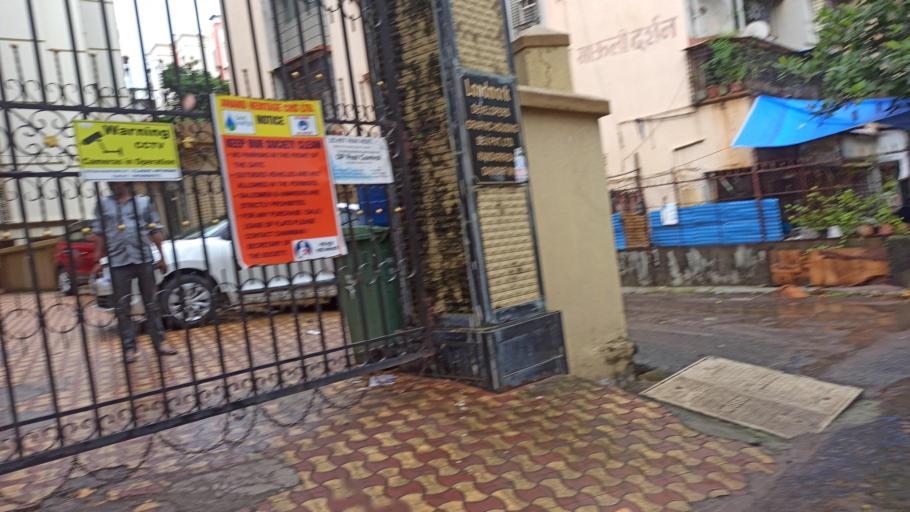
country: IN
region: Maharashtra
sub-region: Mumbai Suburban
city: Borivli
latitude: 19.2595
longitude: 72.8531
